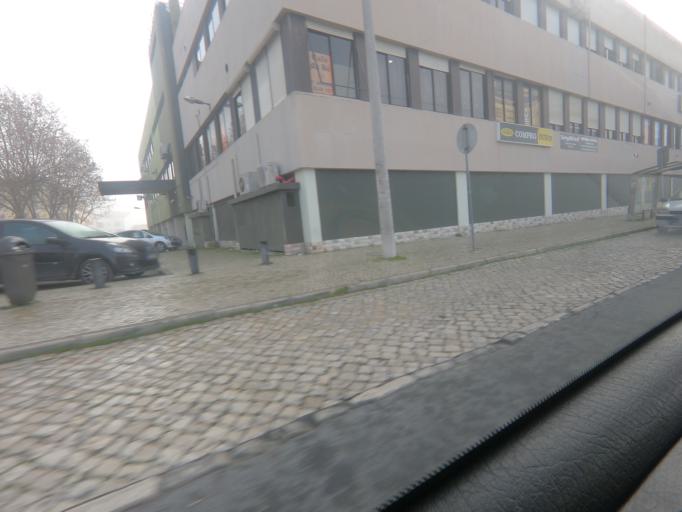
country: PT
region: Setubal
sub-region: Palmela
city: Pinhal Novo
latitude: 38.6344
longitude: -8.9145
